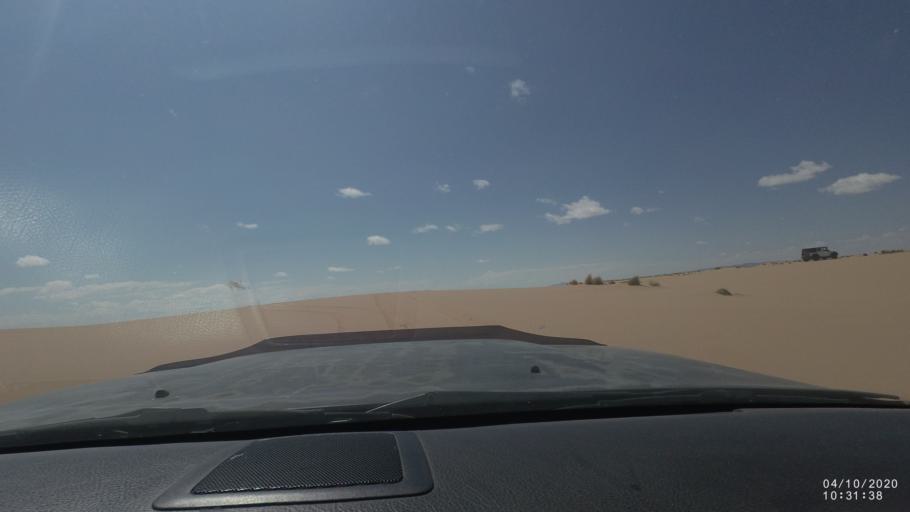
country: BO
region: Oruro
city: Poopo
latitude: -18.7039
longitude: -67.4835
